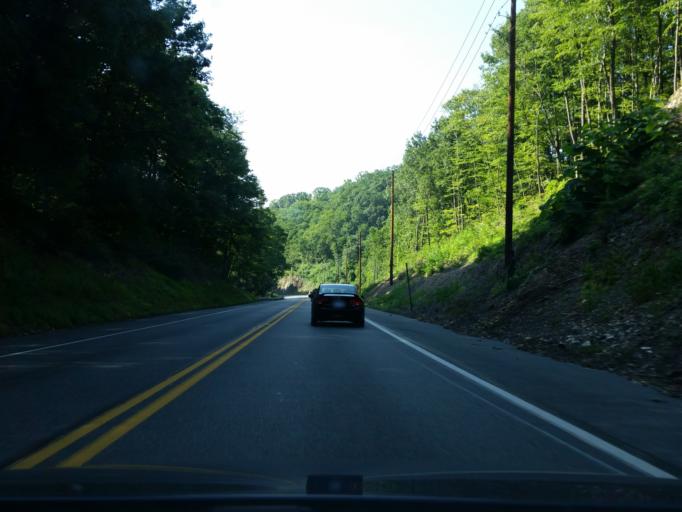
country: US
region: Pennsylvania
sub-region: Lancaster County
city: Columbia
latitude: 40.0495
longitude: -76.5157
